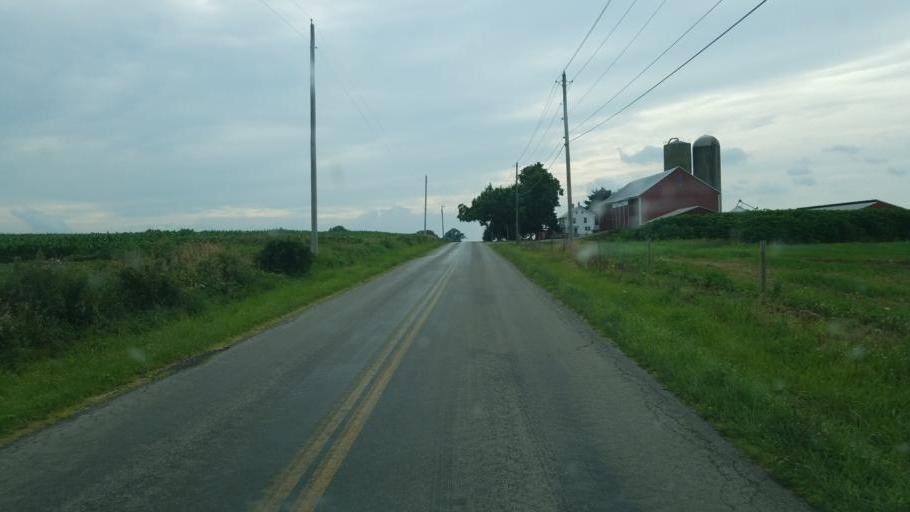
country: US
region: Ohio
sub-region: Wayne County
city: Dalton
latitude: 40.8236
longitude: -81.6718
